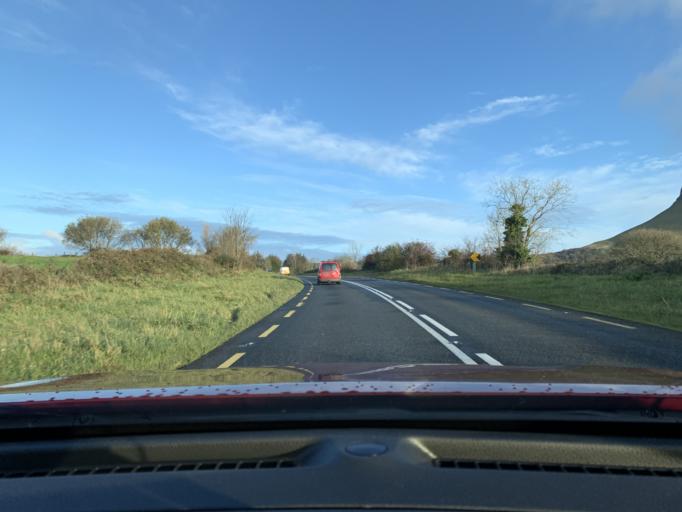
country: IE
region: Connaught
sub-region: Sligo
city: Sligo
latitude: 54.3474
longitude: -8.5040
